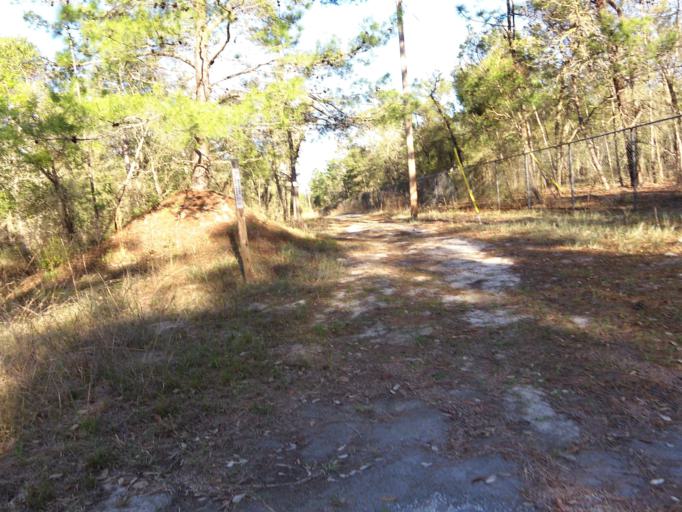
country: US
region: Florida
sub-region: Clay County
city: Keystone Heights
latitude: 29.8179
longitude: -82.0143
